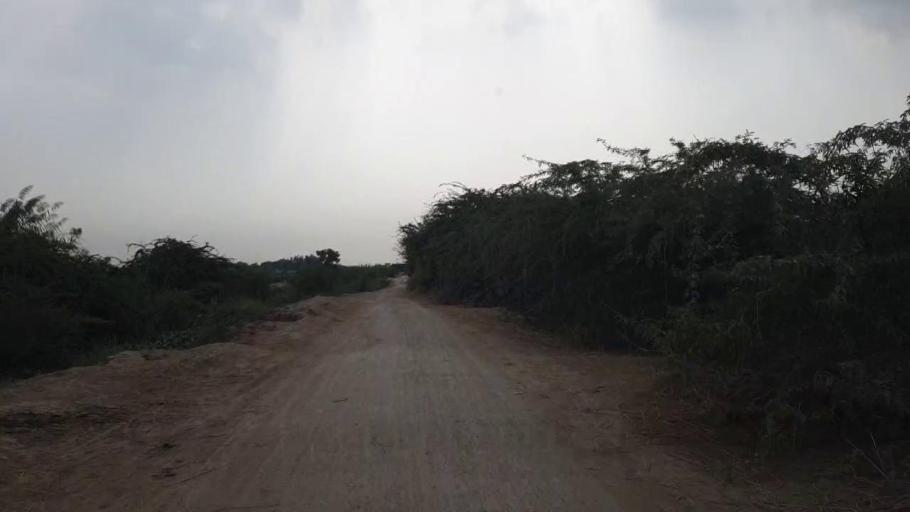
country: PK
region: Sindh
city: Talhar
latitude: 24.9042
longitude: 68.7709
